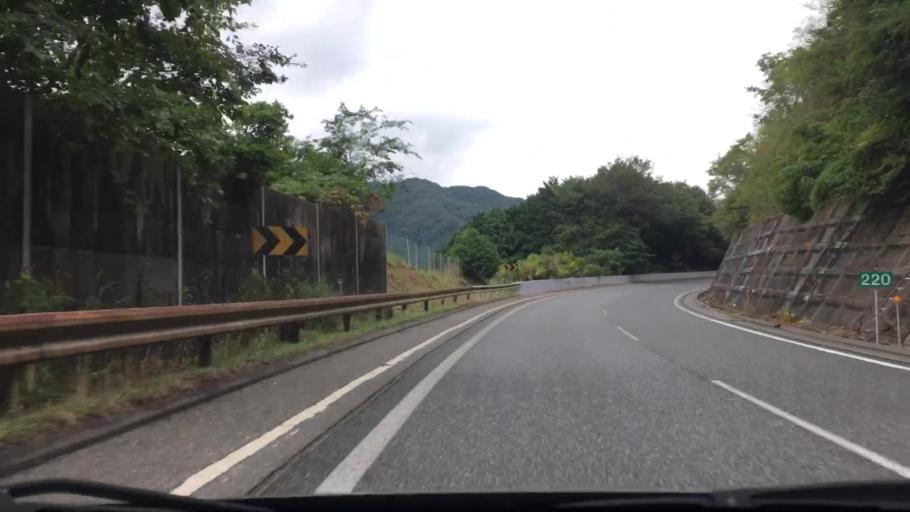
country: JP
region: Okayama
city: Niimi
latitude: 34.9899
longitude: 133.4629
